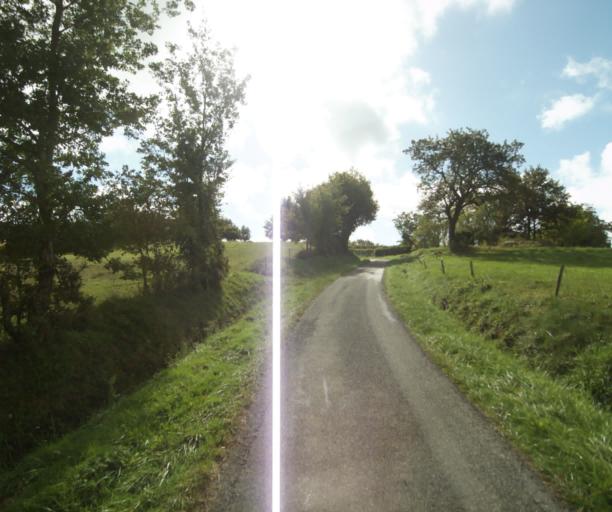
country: FR
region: Midi-Pyrenees
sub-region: Departement du Gers
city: Nogaro
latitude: 43.8337
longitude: -0.0751
